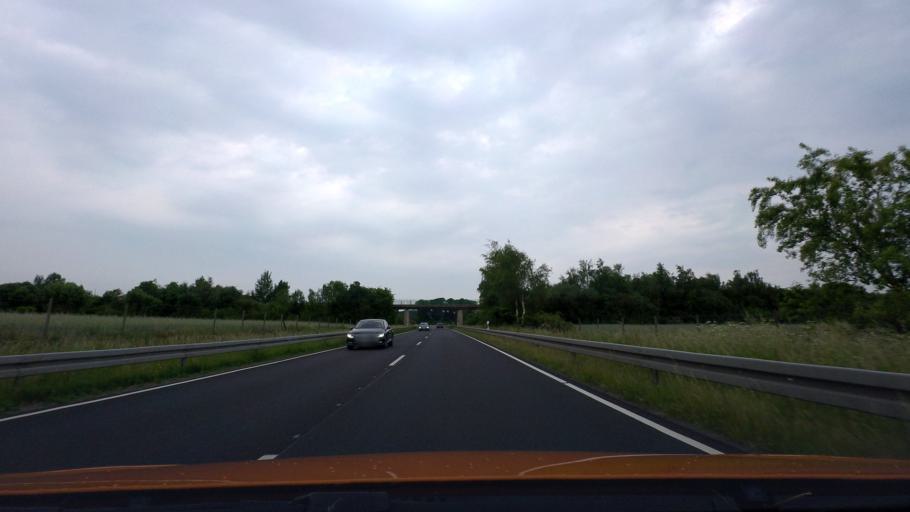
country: DE
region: Lower Saxony
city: Wietzen
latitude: 52.6718
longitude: 9.1054
